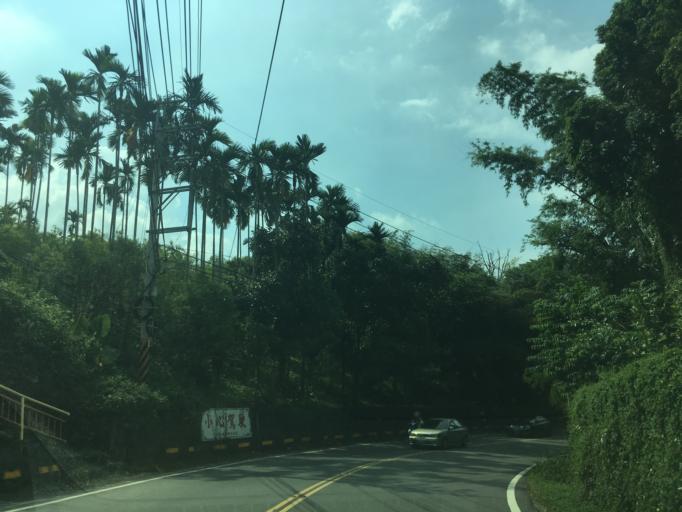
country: TW
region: Taiwan
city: Fengyuan
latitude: 24.2578
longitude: 120.8132
